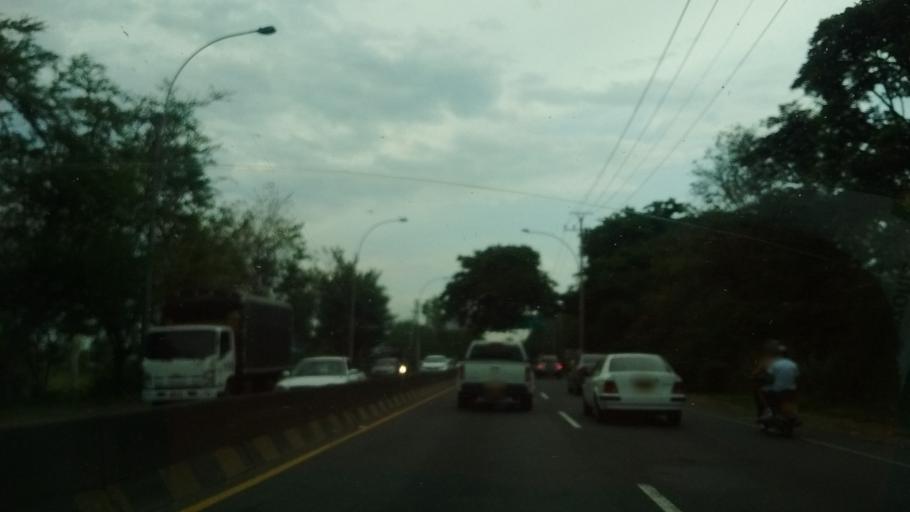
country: CO
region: Valle del Cauca
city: Cali
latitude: 3.3576
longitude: -76.5238
